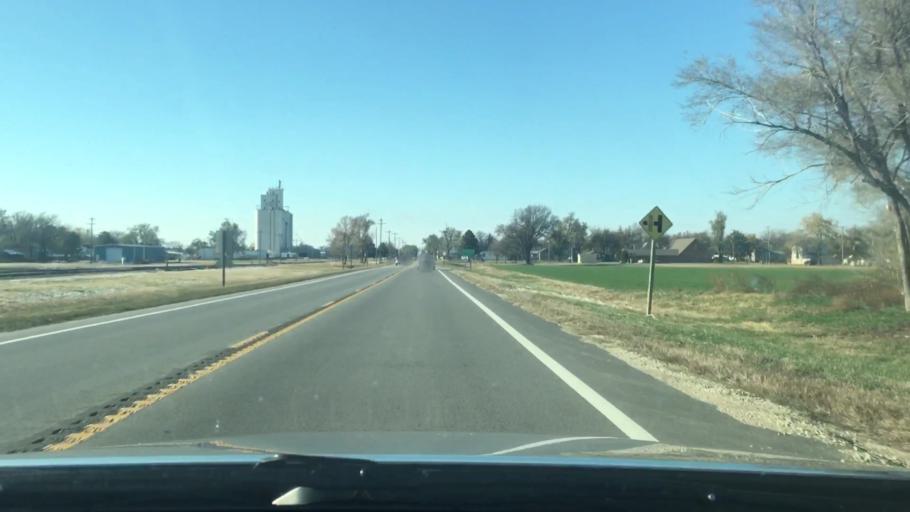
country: US
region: Kansas
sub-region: Reno County
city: Nickerson
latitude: 38.1431
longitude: -98.0775
